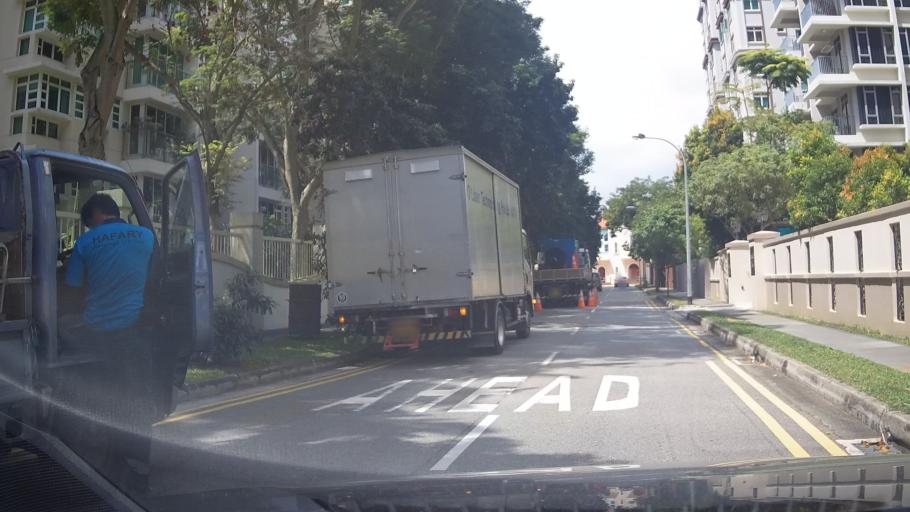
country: SG
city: Singapore
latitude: 1.3126
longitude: 103.8954
